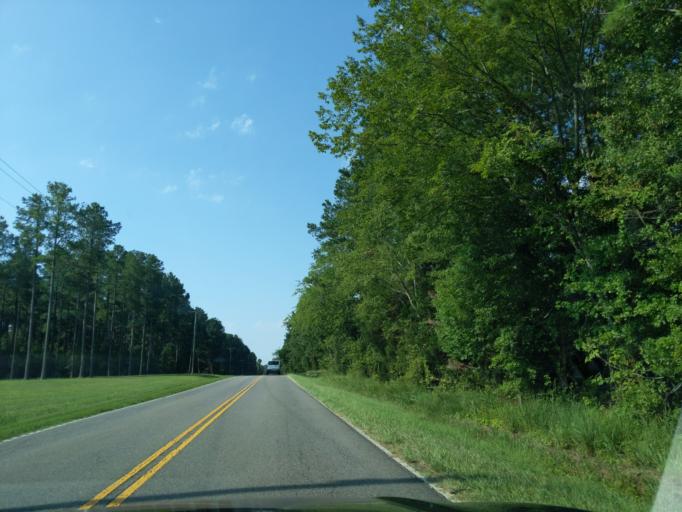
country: US
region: South Carolina
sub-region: Lexington County
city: Leesville
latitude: 33.9776
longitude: -81.5272
